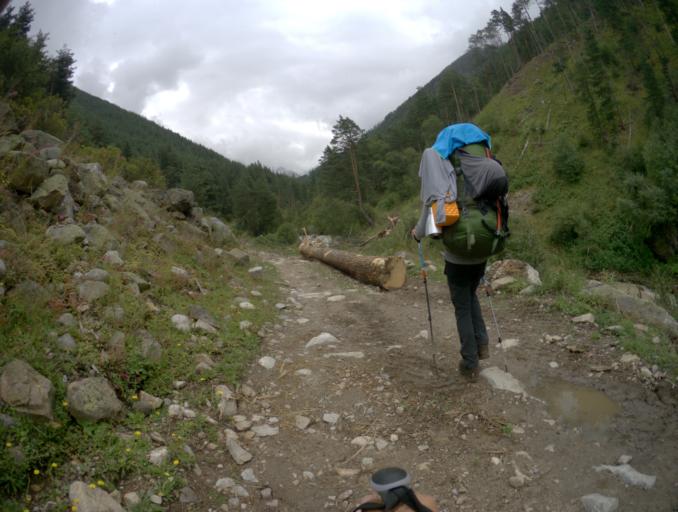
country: RU
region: Karachayevo-Cherkesiya
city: Uchkulan
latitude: 43.4181
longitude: 42.2095
